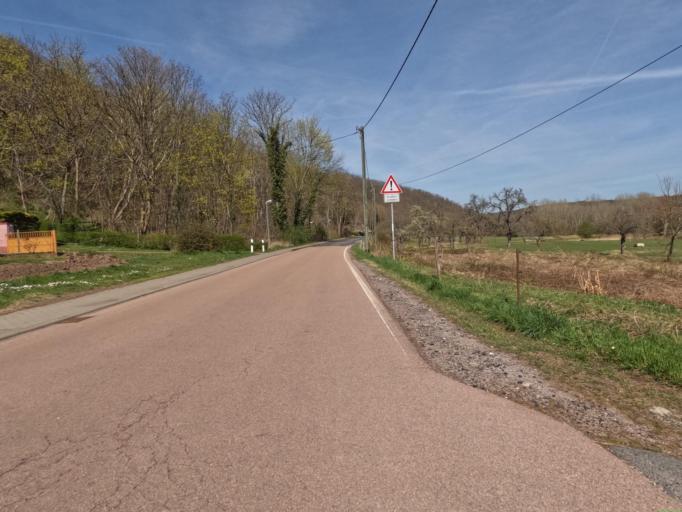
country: DE
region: Saxony-Anhalt
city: Konnern
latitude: 51.6247
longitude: 11.7483
